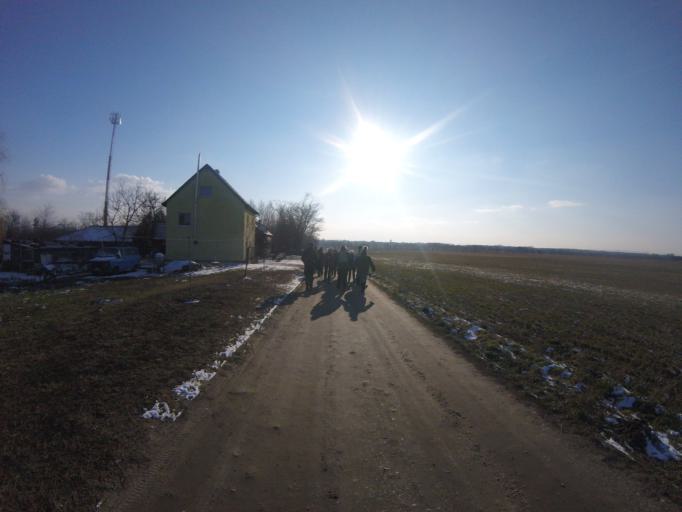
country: HU
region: Pest
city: Ecser
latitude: 47.4548
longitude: 19.2976
